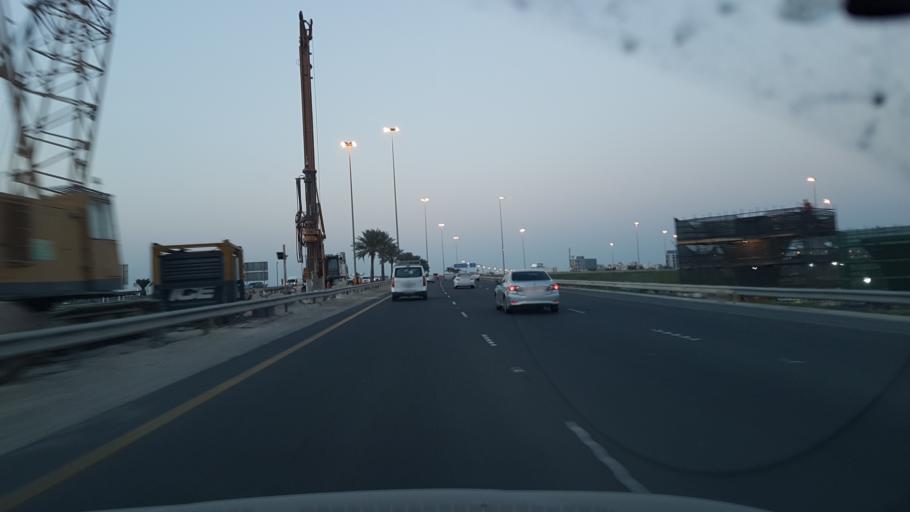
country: BH
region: Northern
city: Madinat `Isa
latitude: 26.1818
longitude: 50.5027
